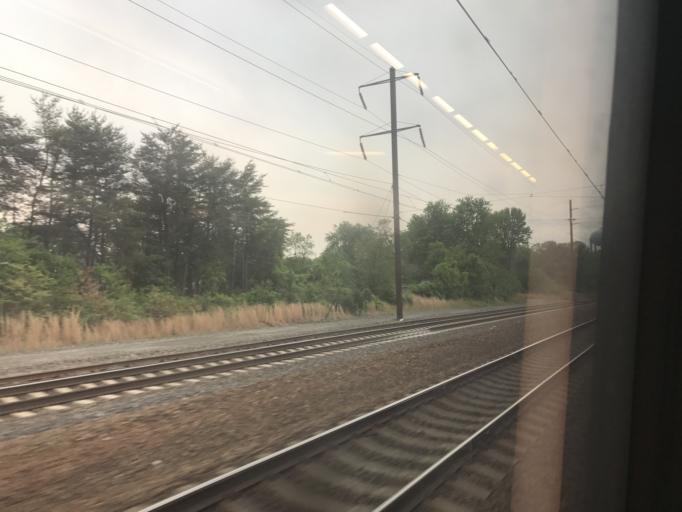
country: US
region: Maryland
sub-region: Anne Arundel County
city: Odenton
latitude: 39.0823
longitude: -76.7094
